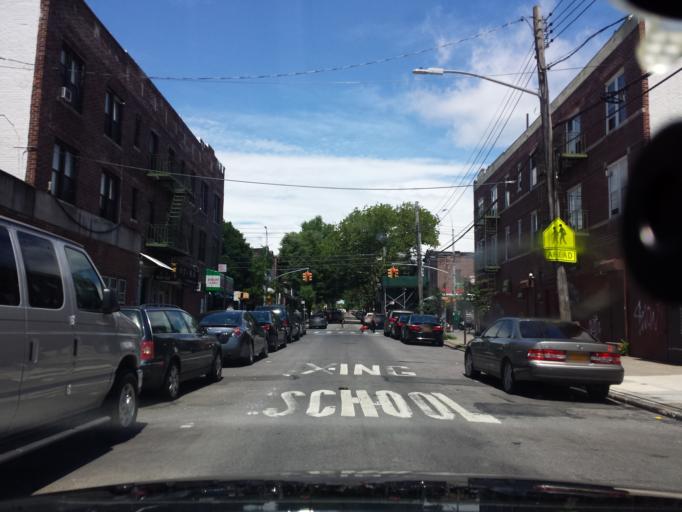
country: US
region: New York
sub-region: Kings County
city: Bensonhurst
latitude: 40.6425
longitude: -74.0014
